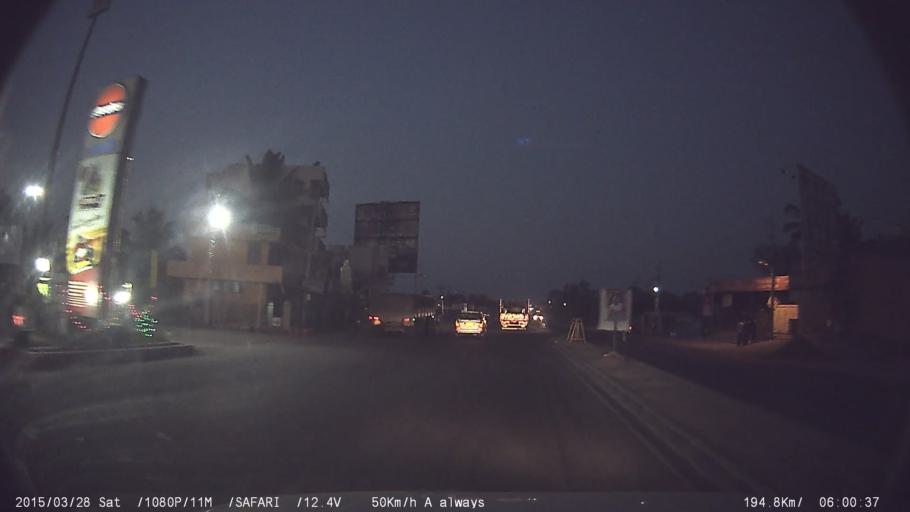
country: IN
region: Karnataka
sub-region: Bangalore Urban
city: Bangalore
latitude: 12.8637
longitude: 77.4343
